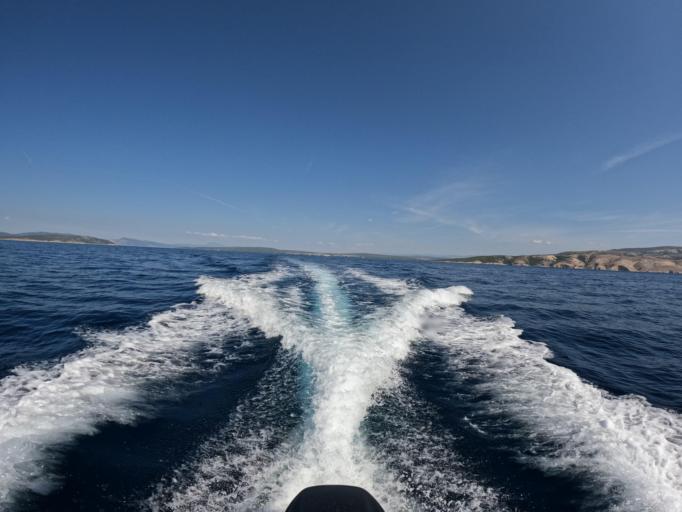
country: HR
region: Primorsko-Goranska
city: Punat
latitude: 44.9458
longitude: 14.6146
